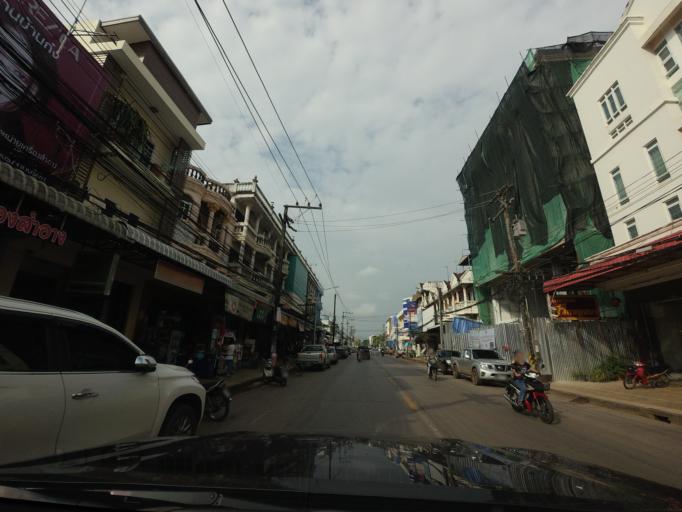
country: TH
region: Nong Khai
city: Nong Khai
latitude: 17.8816
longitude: 102.7468
